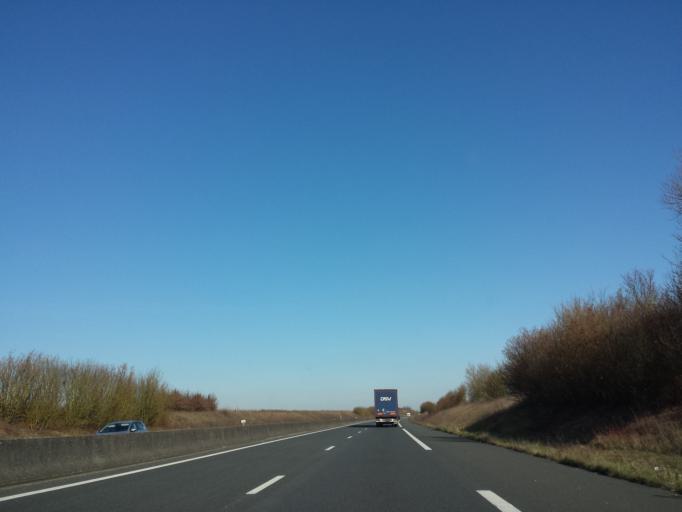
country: FR
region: Picardie
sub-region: Departement de l'Oise
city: Tille
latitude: 49.4853
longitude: 2.1654
